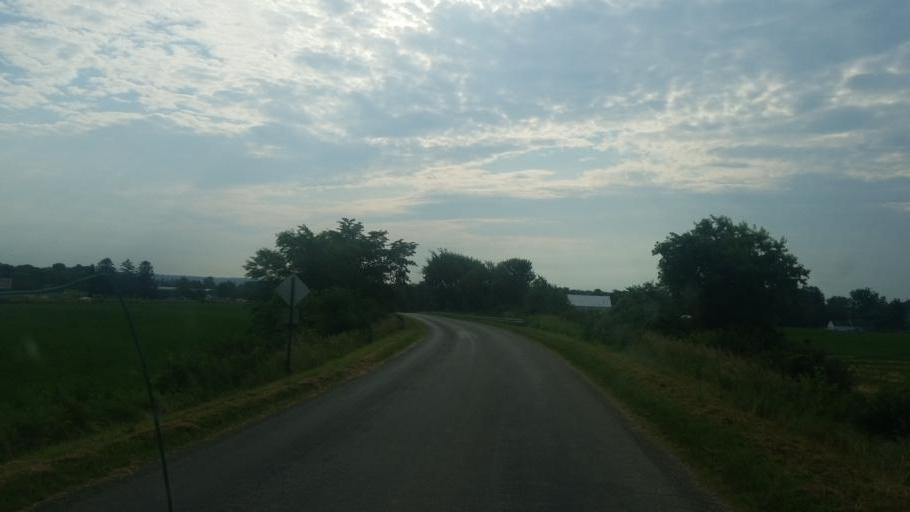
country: US
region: Ohio
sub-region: Wayne County
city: Wooster
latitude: 40.7980
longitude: -82.0272
